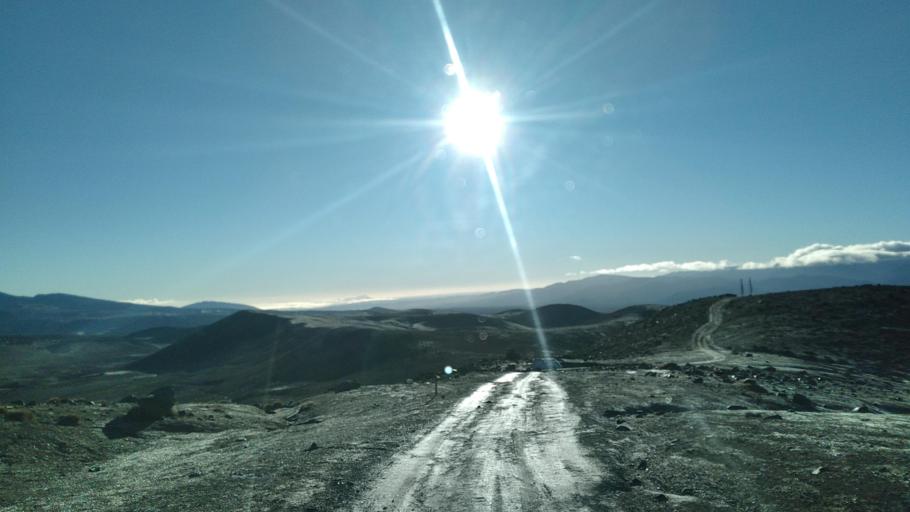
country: NZ
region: Manawatu-Wanganui
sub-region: Ruapehu District
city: Waiouru
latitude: -39.2692
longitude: 175.6498
